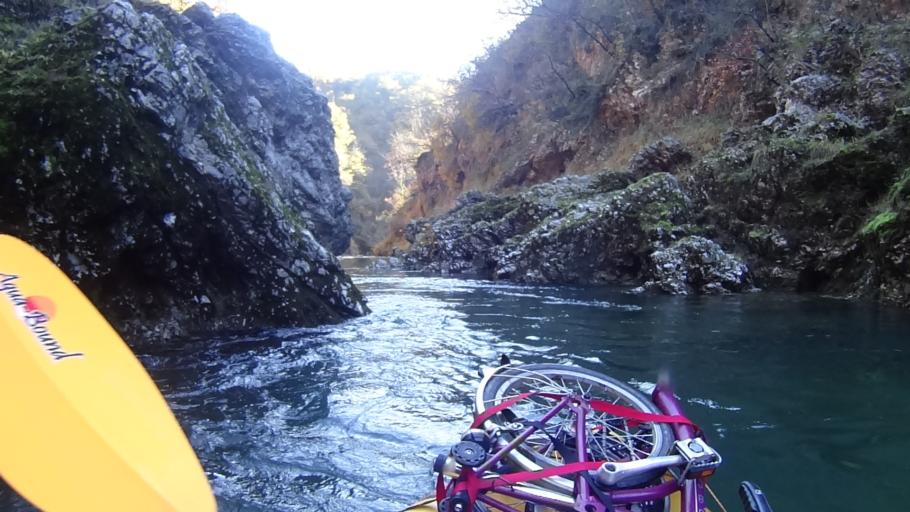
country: IT
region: Veneto
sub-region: Provincia di Vicenza
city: Cogollo del Cengio
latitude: 45.7739
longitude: 11.4219
